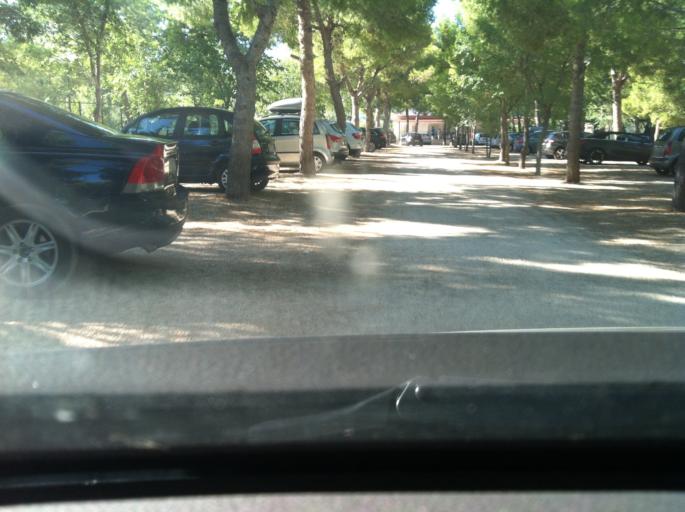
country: IT
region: Apulia
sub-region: Provincia di Foggia
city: Monte Sant'Angelo
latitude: 41.6554
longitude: 15.9768
